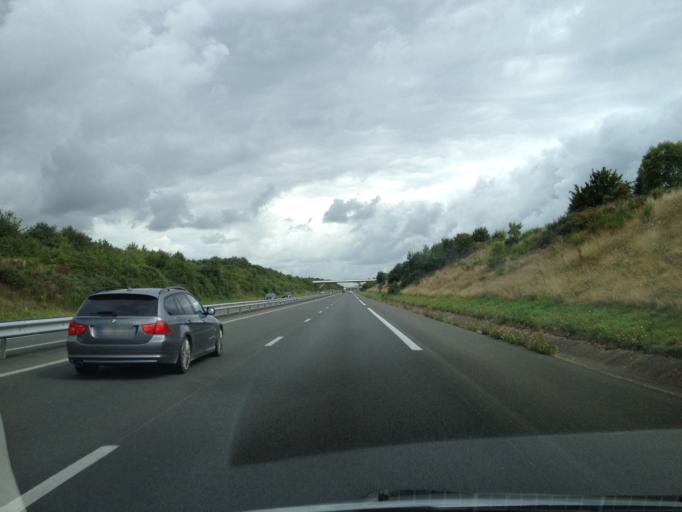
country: FR
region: Pays de la Loire
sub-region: Departement de la Vendee
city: Saint-Martin-des-Noyers
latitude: 46.7139
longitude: -1.1568
